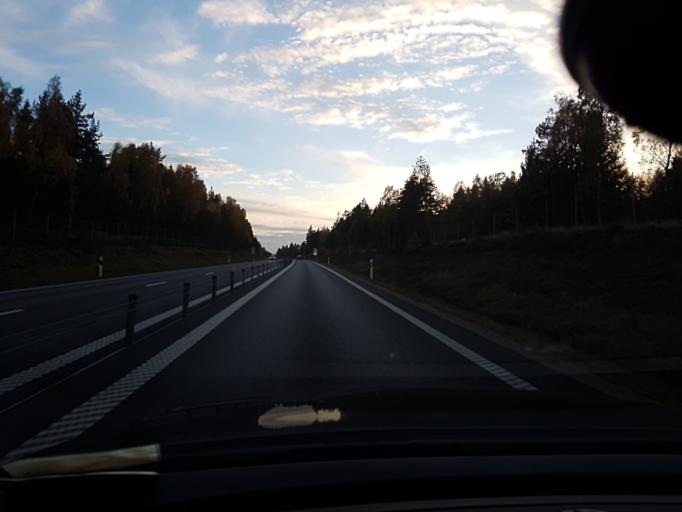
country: SE
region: Kronoberg
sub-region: Ljungby Kommun
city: Ljungby
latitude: 56.7837
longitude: 13.8238
